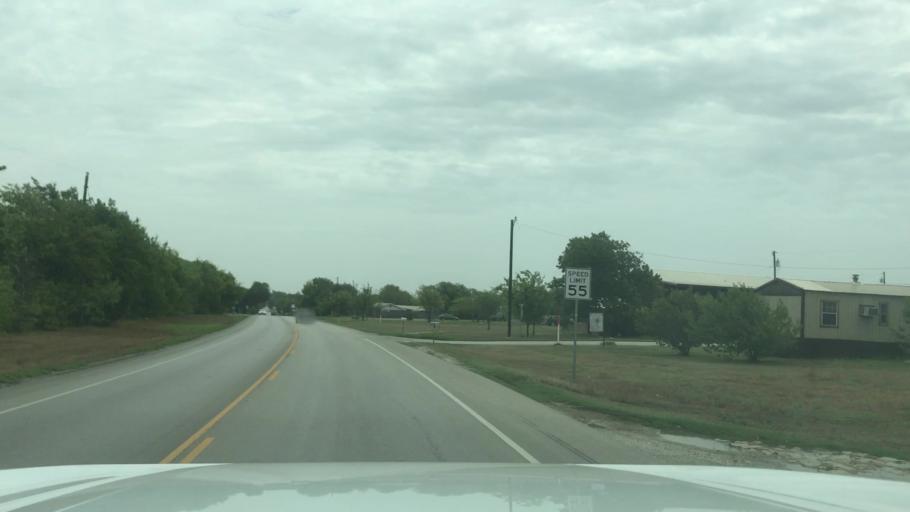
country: US
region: Texas
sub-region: Erath County
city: Dublin
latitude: 32.0886
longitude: -98.3571
